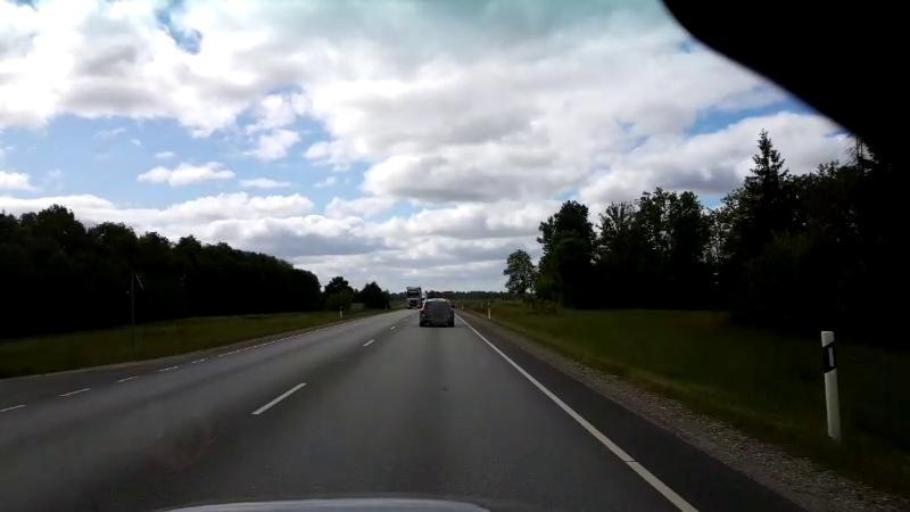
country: EE
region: Paernumaa
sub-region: Halinga vald
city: Parnu-Jaagupi
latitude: 58.5738
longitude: 24.5123
